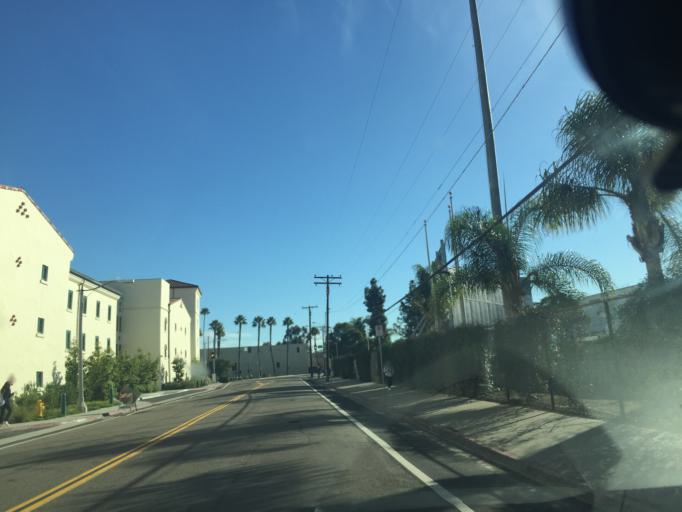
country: US
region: California
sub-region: San Diego County
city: La Mesa
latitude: 32.7753
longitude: -117.0785
